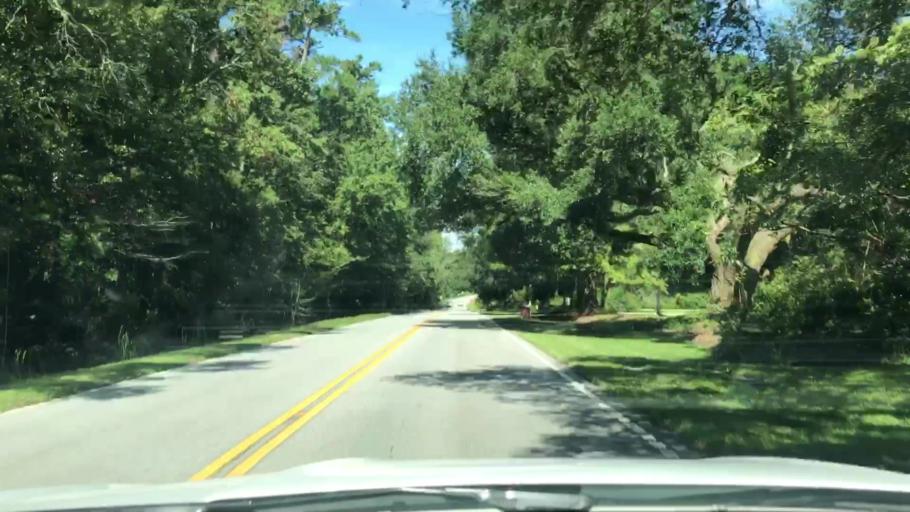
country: US
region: South Carolina
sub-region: Dorchester County
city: Centerville
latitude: 32.9457
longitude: -80.1972
